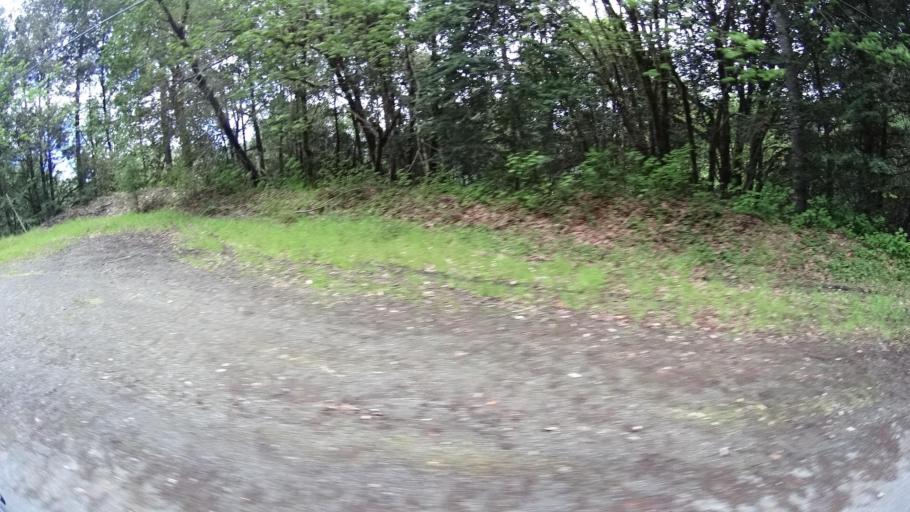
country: US
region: California
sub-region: Humboldt County
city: Blue Lake
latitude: 40.7591
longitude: -123.9089
